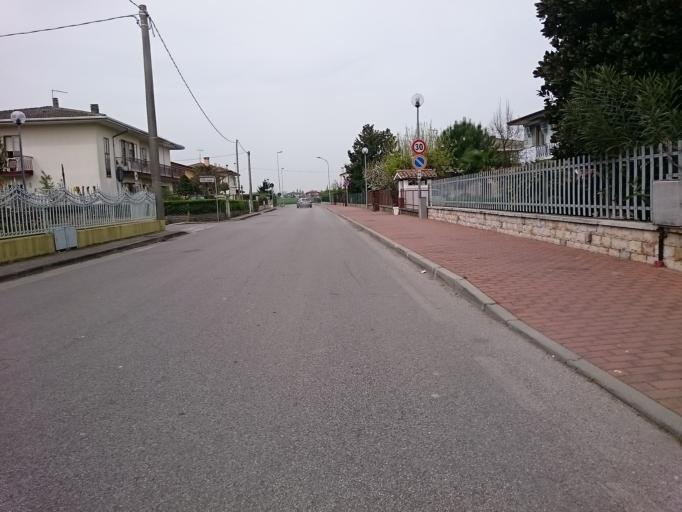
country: IT
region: Veneto
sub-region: Provincia di Padova
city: Bagnoli di Sopra
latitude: 45.1873
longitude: 11.8833
